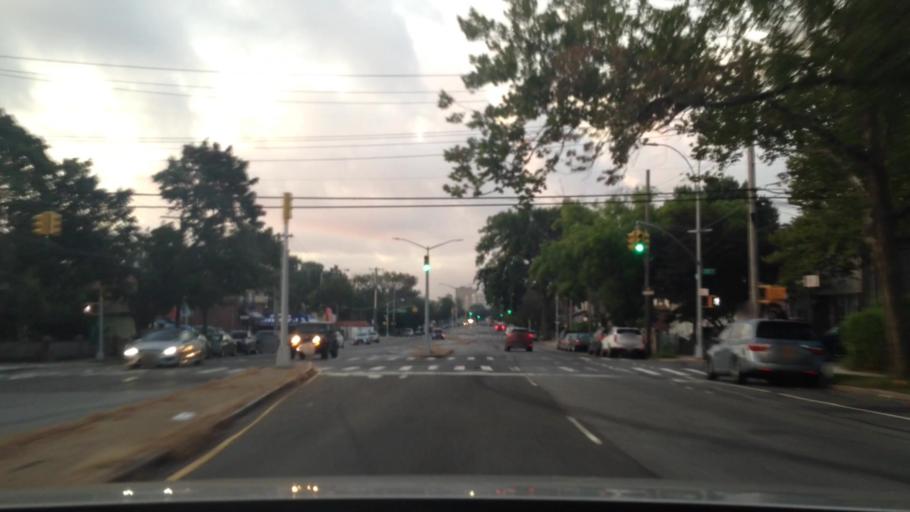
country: US
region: New York
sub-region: Queens County
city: Jamaica
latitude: 40.7275
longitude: -73.8052
